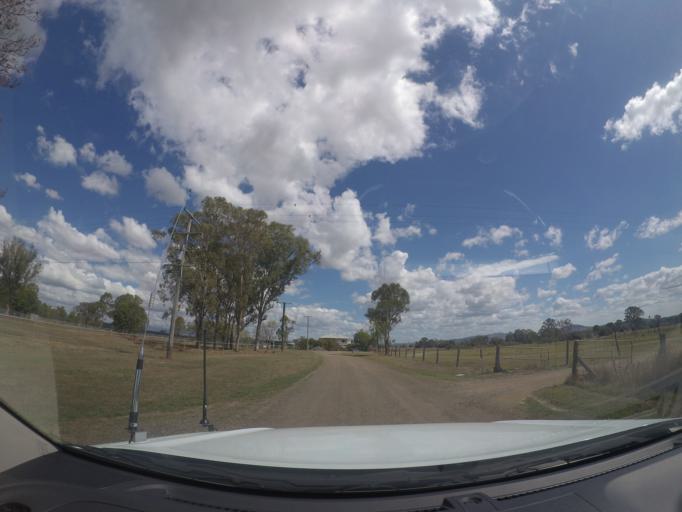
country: AU
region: Queensland
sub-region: Logan
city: Cedar Vale
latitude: -27.8968
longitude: 152.9584
